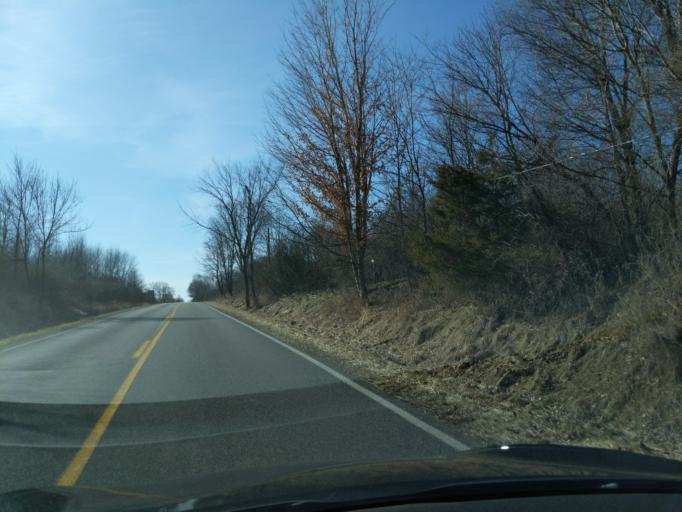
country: US
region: Michigan
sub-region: Ionia County
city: Saranac
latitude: 42.9297
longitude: -85.1363
